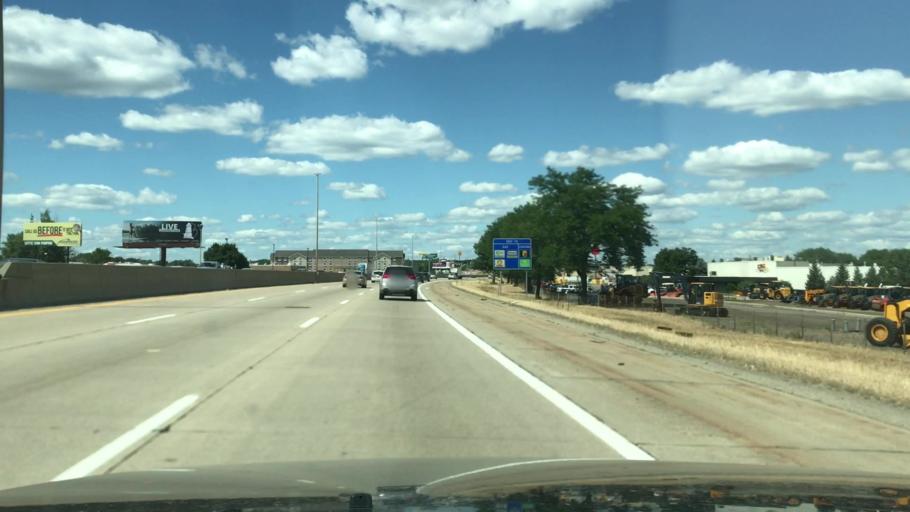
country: US
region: Michigan
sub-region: Kent County
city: Kentwood
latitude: 42.8772
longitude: -85.6819
